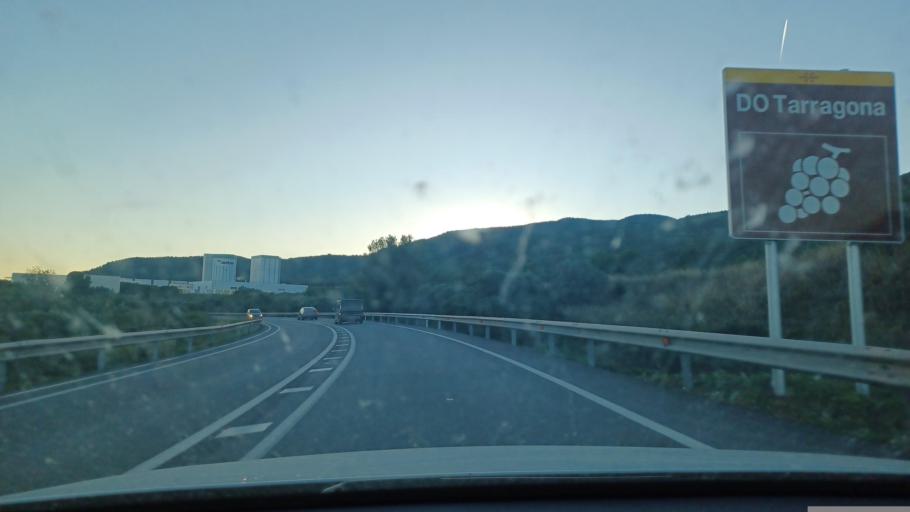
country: ES
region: Catalonia
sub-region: Provincia de Tarragona
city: Alcover
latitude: 41.2855
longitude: 1.1854
